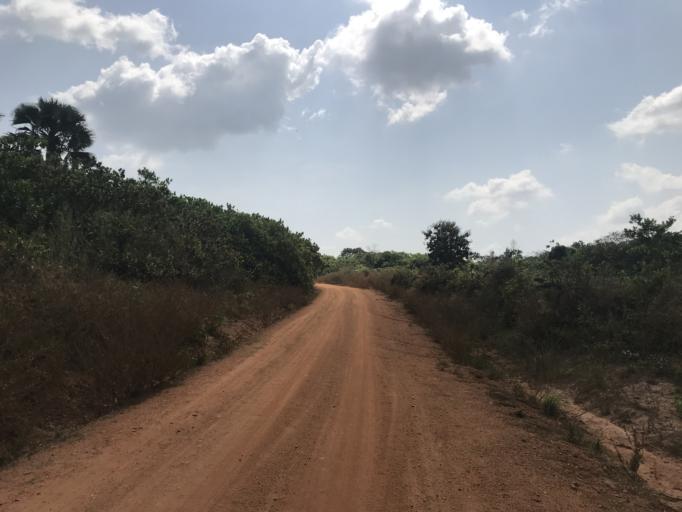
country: NG
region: Osun
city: Ifon
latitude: 7.9902
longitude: 4.5162
